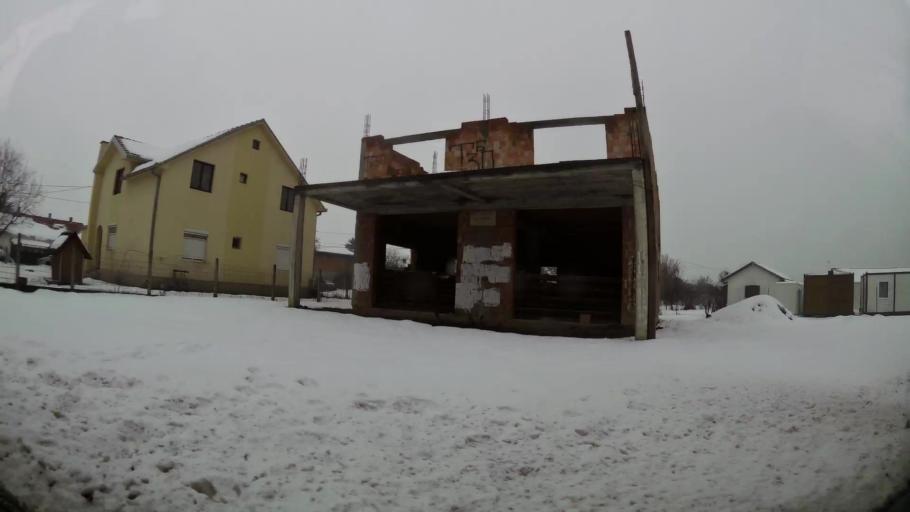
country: RS
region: Central Serbia
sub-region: Belgrade
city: Surcin
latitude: 44.8659
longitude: 20.3202
